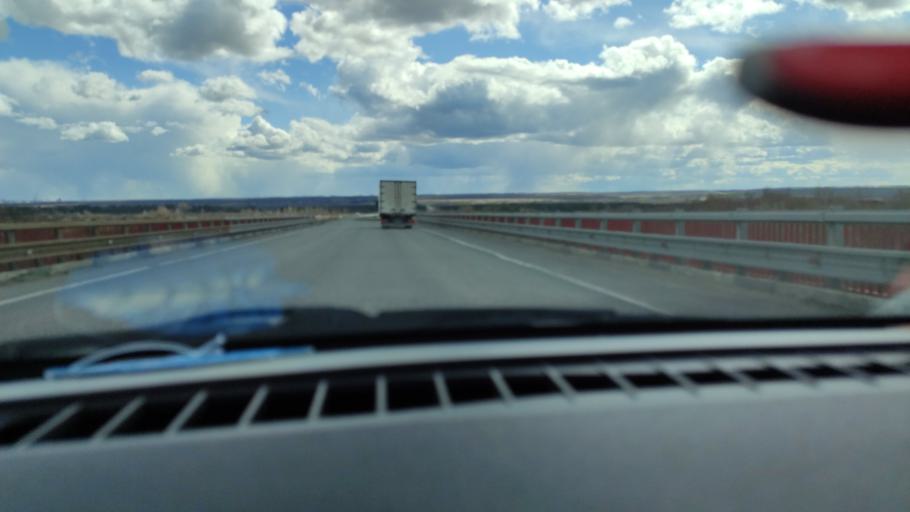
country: RU
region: Samara
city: Varlamovo
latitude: 53.1609
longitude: 48.2835
